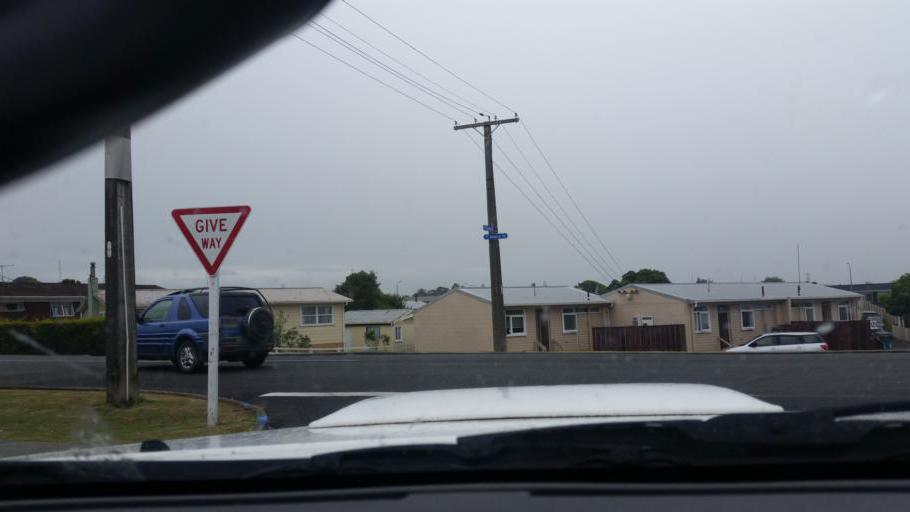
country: NZ
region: Northland
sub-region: Kaipara District
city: Dargaville
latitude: -35.9337
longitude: 173.8723
